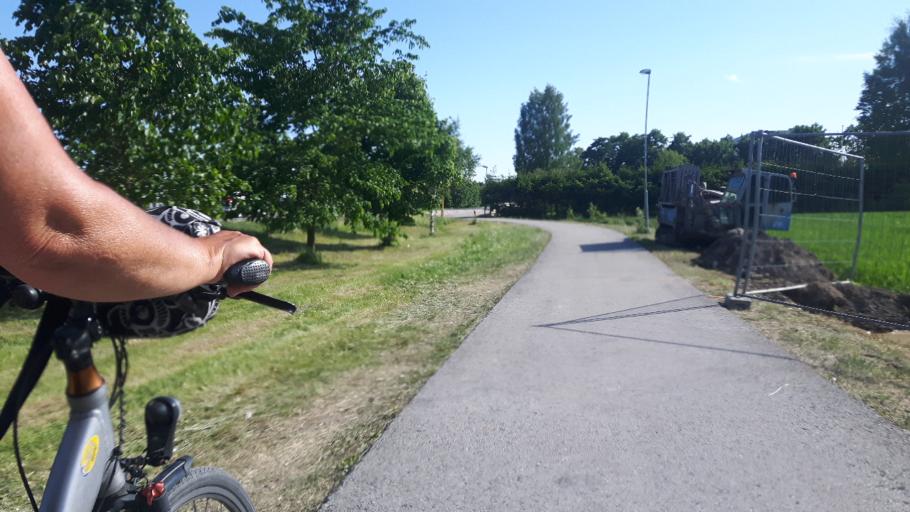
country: EE
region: Raplamaa
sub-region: Kehtna vald
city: Kehtna
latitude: 58.9302
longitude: 24.8782
